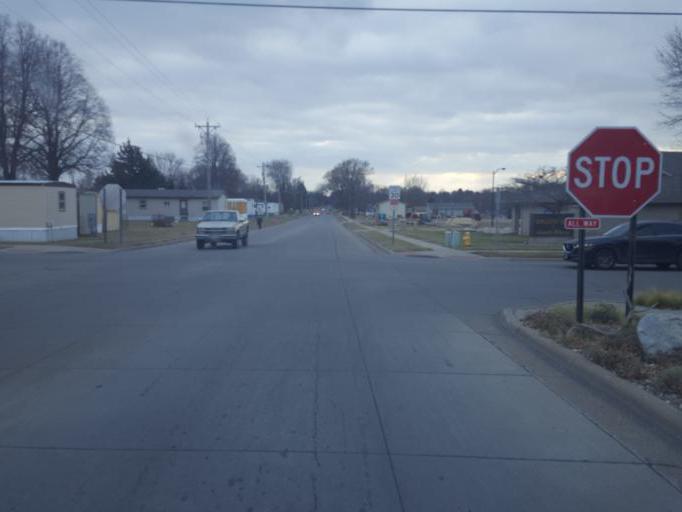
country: US
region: South Dakota
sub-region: Yankton County
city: Yankton
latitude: 42.8946
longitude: -97.3921
